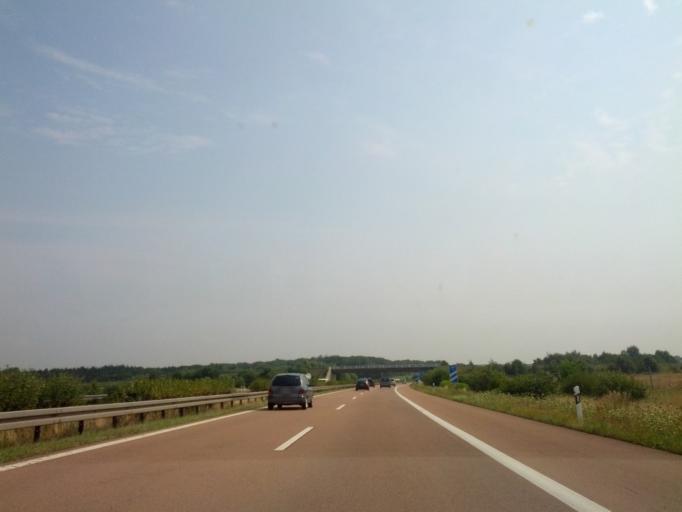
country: DE
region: Mecklenburg-Vorpommern
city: Tessin
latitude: 54.0325
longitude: 12.4035
